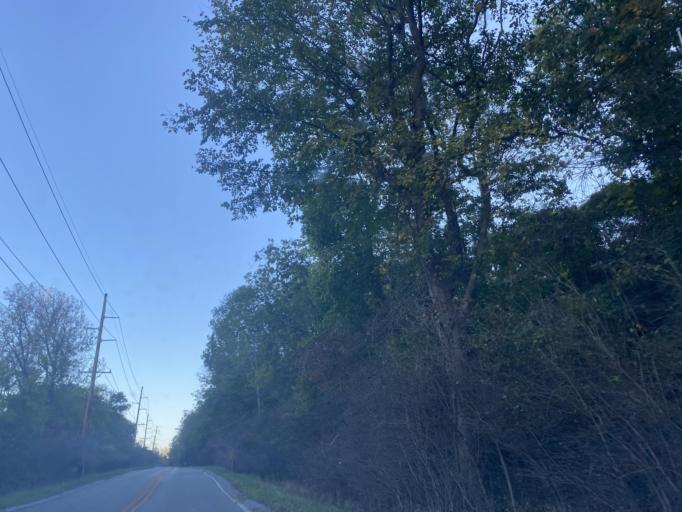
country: US
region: Kentucky
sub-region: Campbell County
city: Fort Thomas
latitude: 39.1045
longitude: -84.4430
